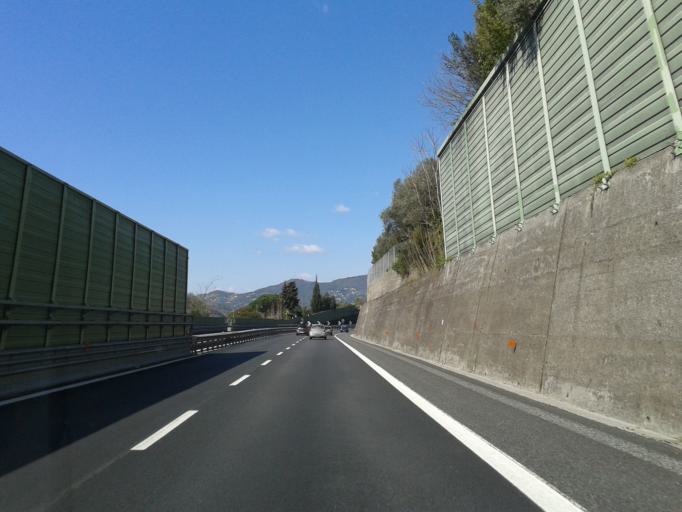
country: IT
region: Liguria
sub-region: Provincia di Genova
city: Zoagli
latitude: 44.3489
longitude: 9.2521
